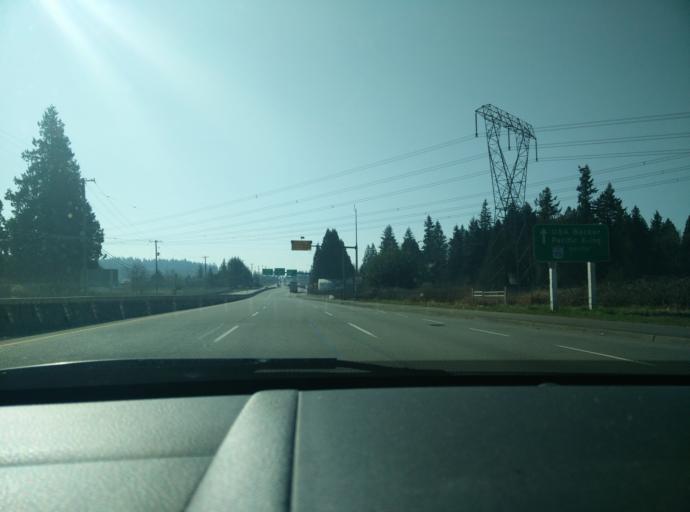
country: US
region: Washington
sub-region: Whatcom County
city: Blaine
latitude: 49.0134
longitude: -122.7354
